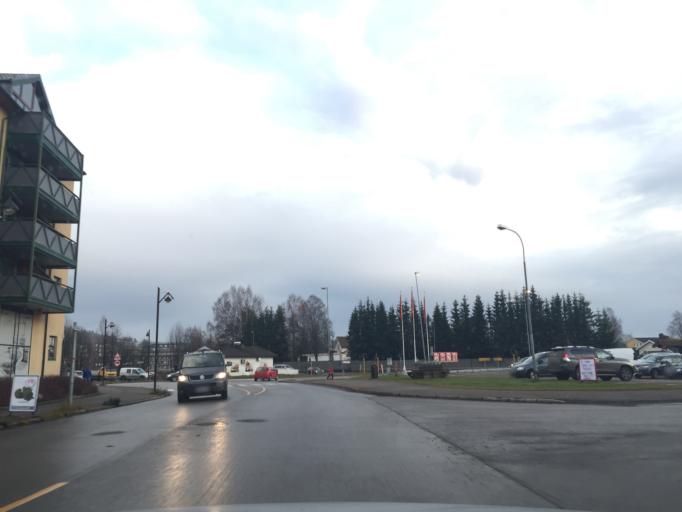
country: NO
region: Hedmark
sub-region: Elverum
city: Elverum
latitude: 60.8821
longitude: 11.5526
